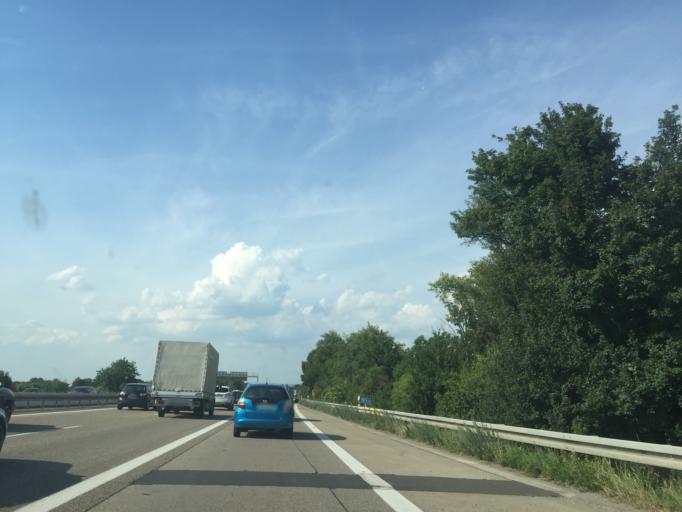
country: DE
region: Baden-Wuerttemberg
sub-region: Karlsruhe Region
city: Eppelheim
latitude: 49.4235
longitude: 8.6343
